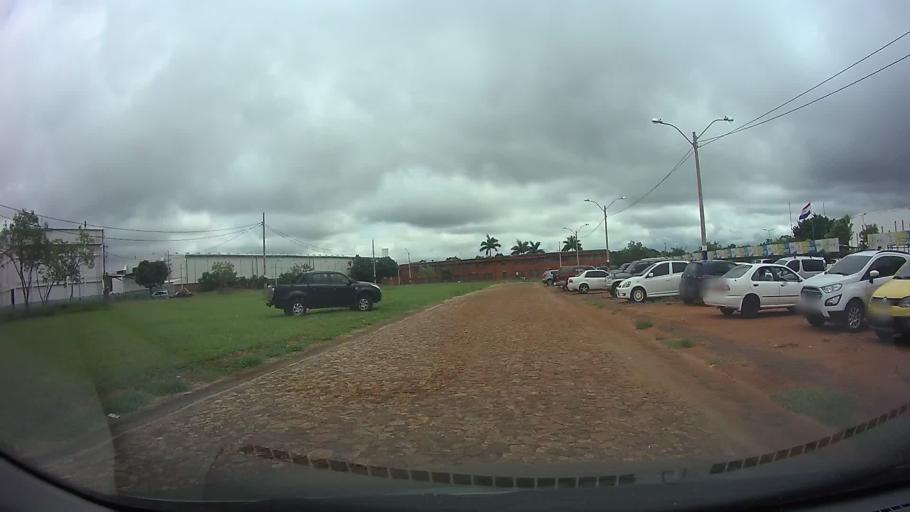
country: PY
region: Central
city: San Lorenzo
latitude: -25.2840
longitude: -57.4889
